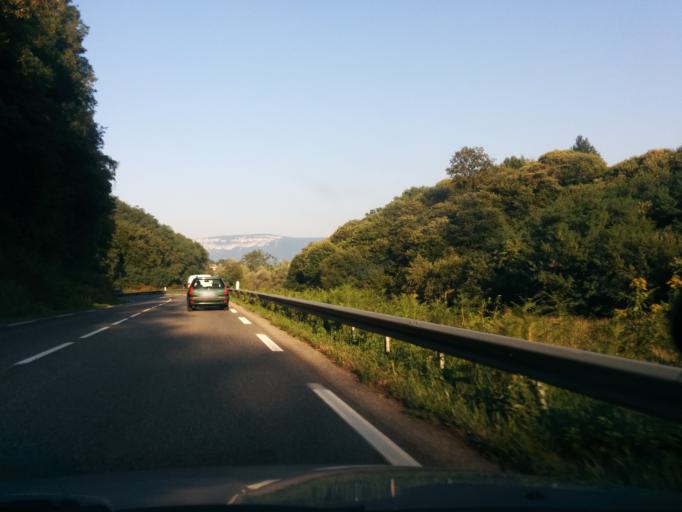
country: FR
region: Rhone-Alpes
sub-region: Departement de l'Isere
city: Les Abrets
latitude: 45.5316
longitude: 5.6196
